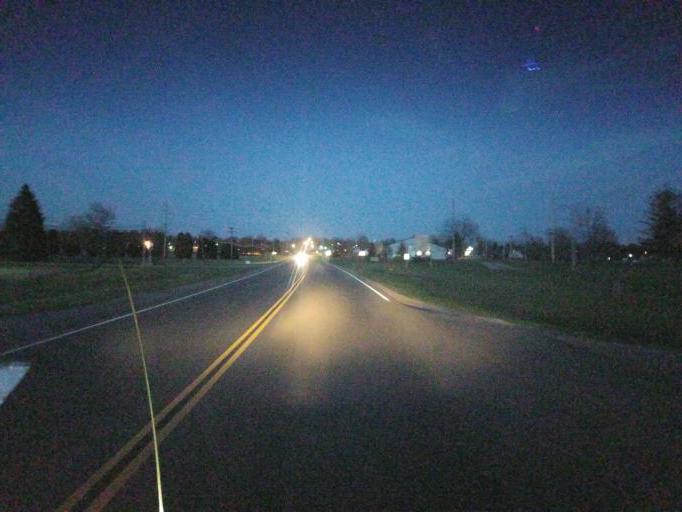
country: US
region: Ohio
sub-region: Logan County
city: Bellefontaine
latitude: 40.3627
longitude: -83.7852
